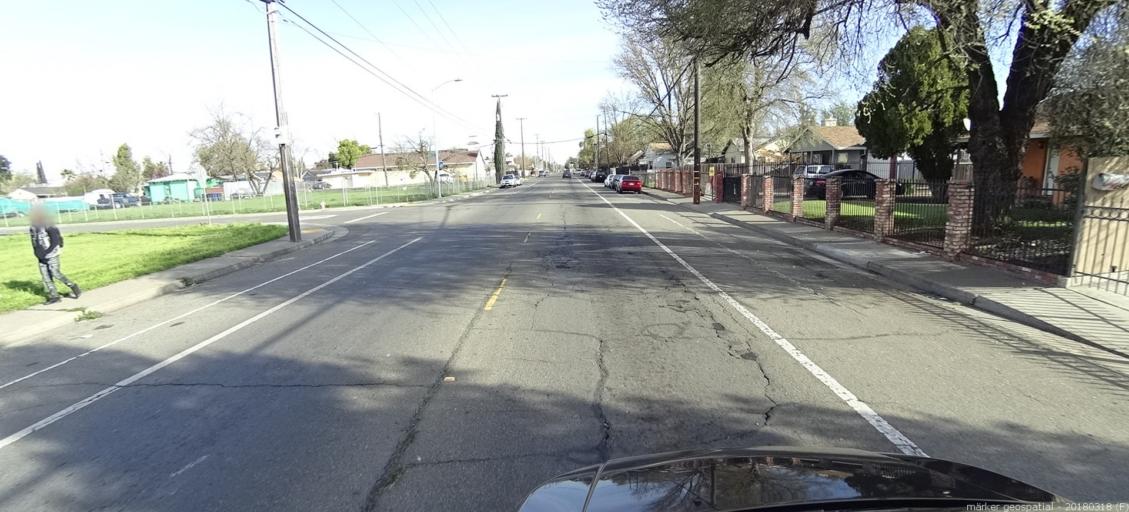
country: US
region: California
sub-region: Sacramento County
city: Parkway
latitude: 38.5308
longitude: -121.4647
